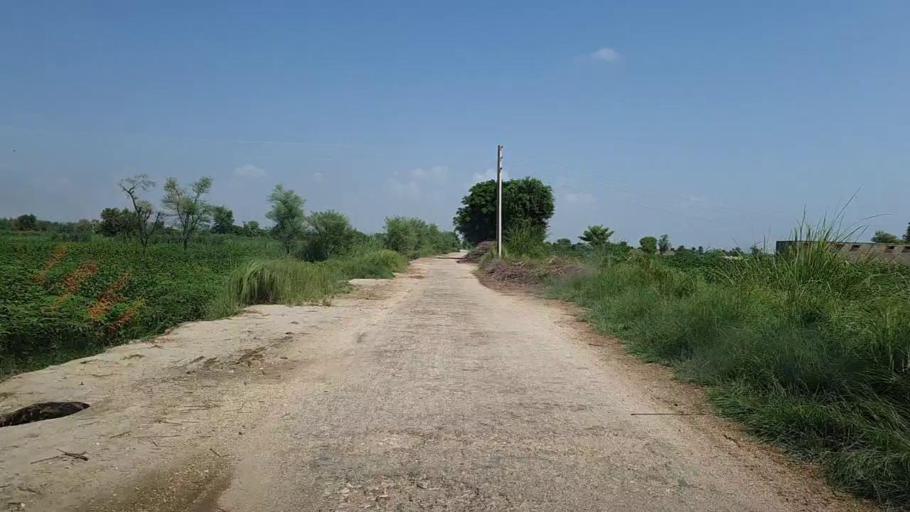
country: PK
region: Sindh
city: Bhiria
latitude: 26.8761
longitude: 68.2478
